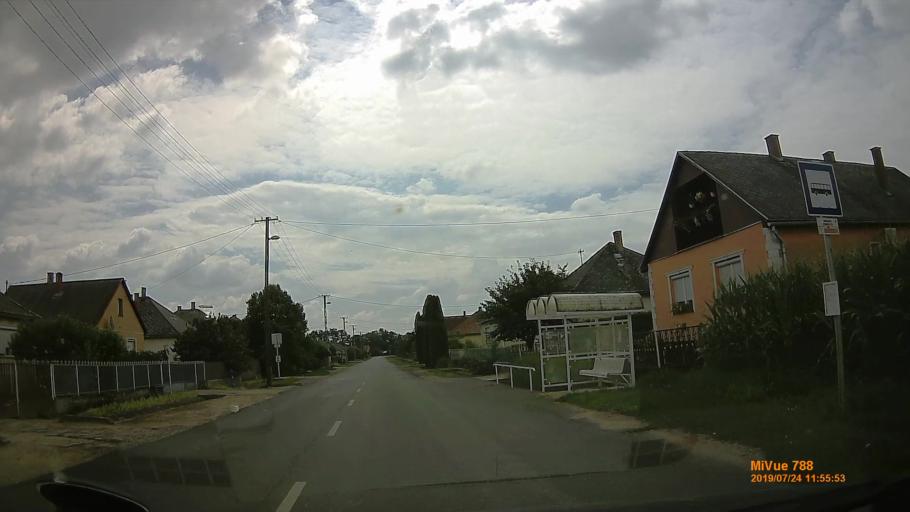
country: HU
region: Szabolcs-Szatmar-Bereg
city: Vasarosnameny
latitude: 48.2050
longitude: 22.4139
